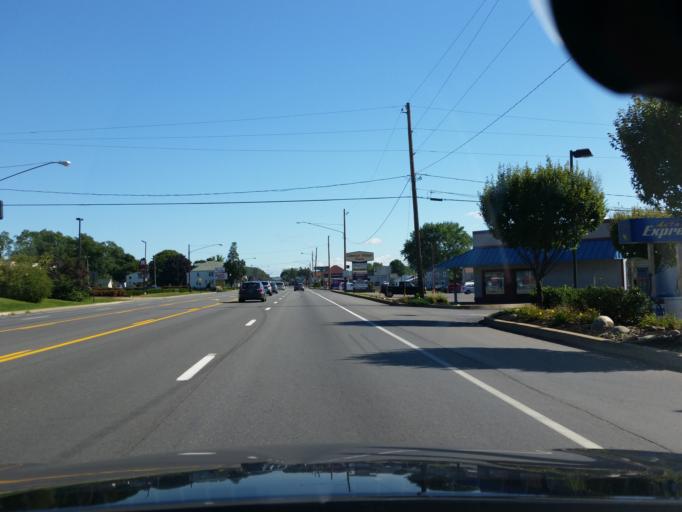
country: US
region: Pennsylvania
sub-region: Snyder County
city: Shamokin Dam
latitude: 40.8422
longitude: -76.8269
